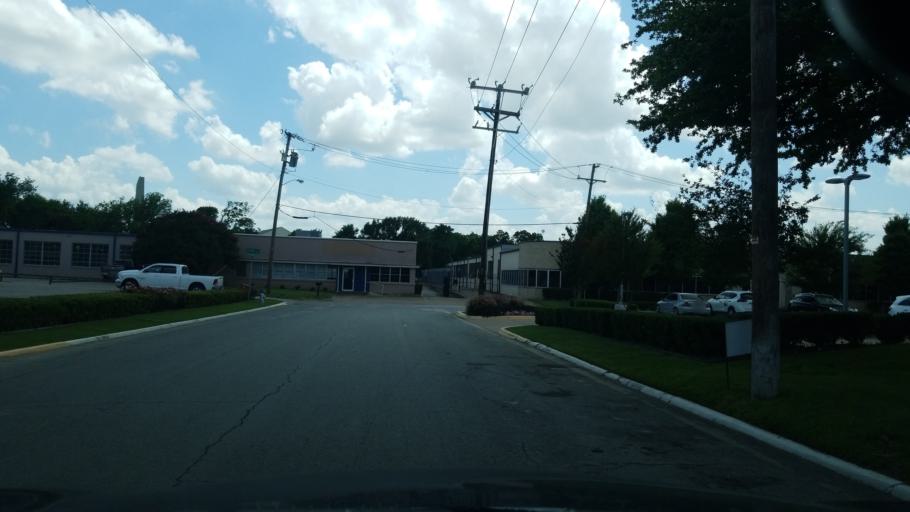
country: US
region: Texas
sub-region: Dallas County
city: University Park
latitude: 32.8302
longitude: -96.8308
